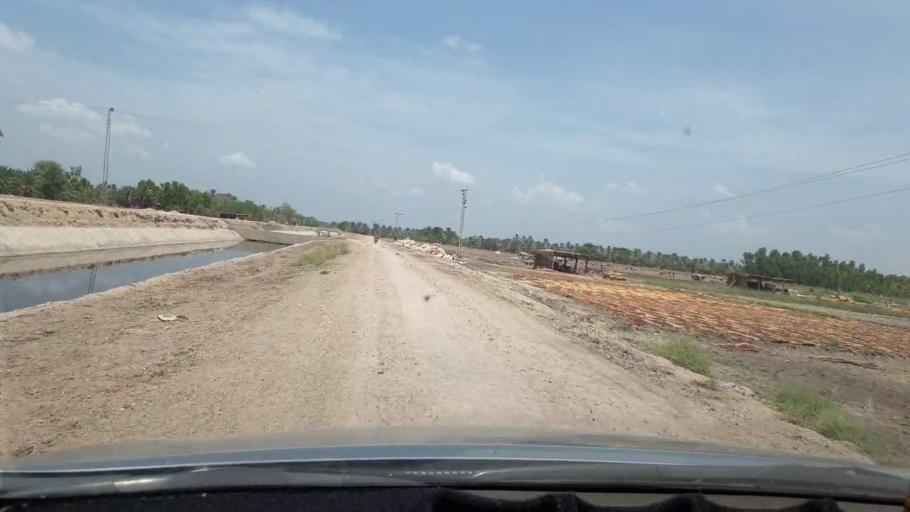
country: PK
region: Sindh
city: Khairpur
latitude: 27.4339
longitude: 68.7816
